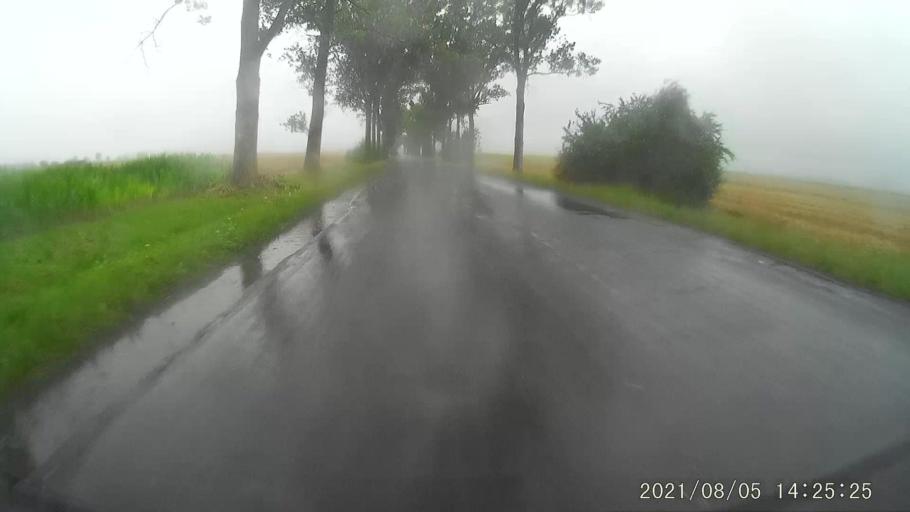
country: PL
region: Opole Voivodeship
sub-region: Powiat nyski
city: Korfantow
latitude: 50.4828
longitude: 17.6160
